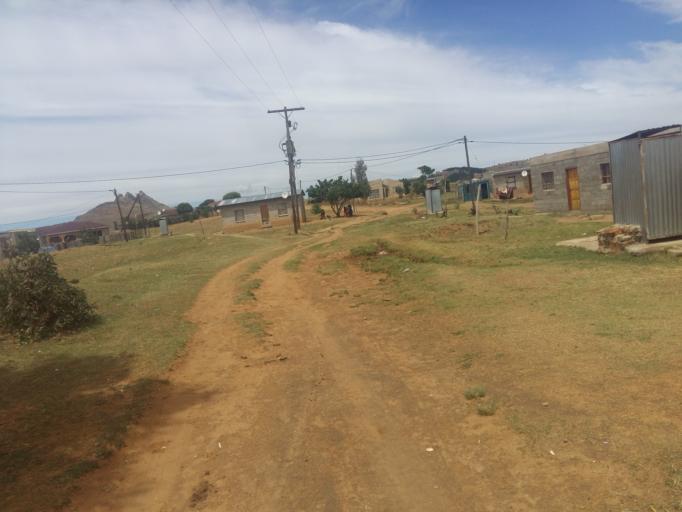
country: LS
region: Mafeteng
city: Mafeteng
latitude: -29.7054
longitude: 27.4301
